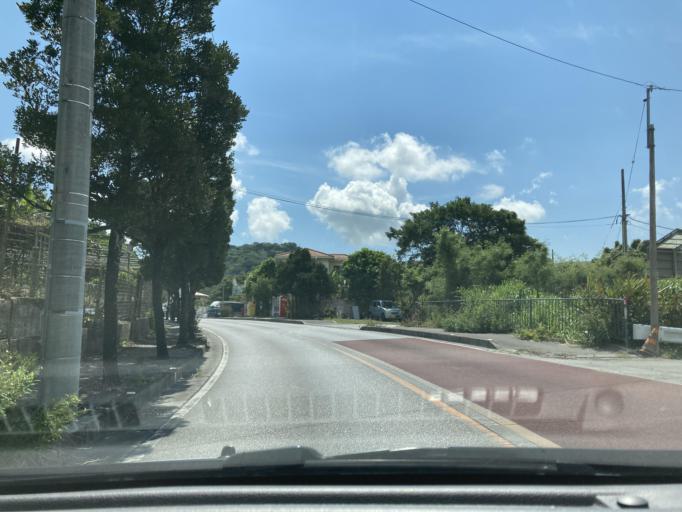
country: JP
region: Okinawa
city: Tomigusuku
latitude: 26.1712
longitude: 127.7529
